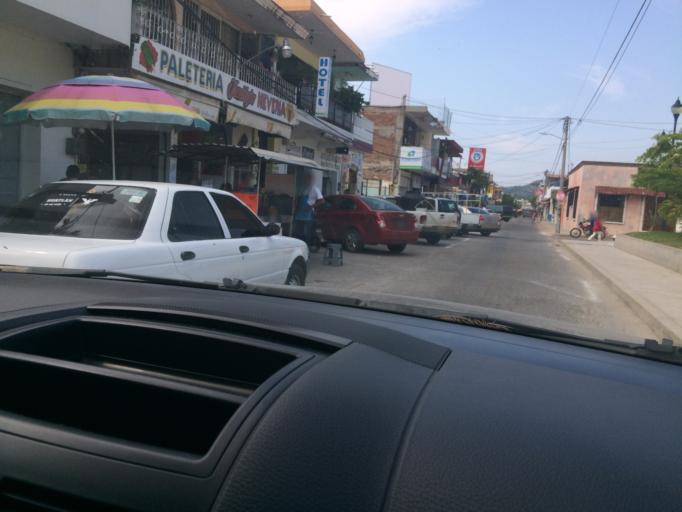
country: MX
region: Jalisco
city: Cihuatlan
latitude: 19.2379
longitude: -104.5571
